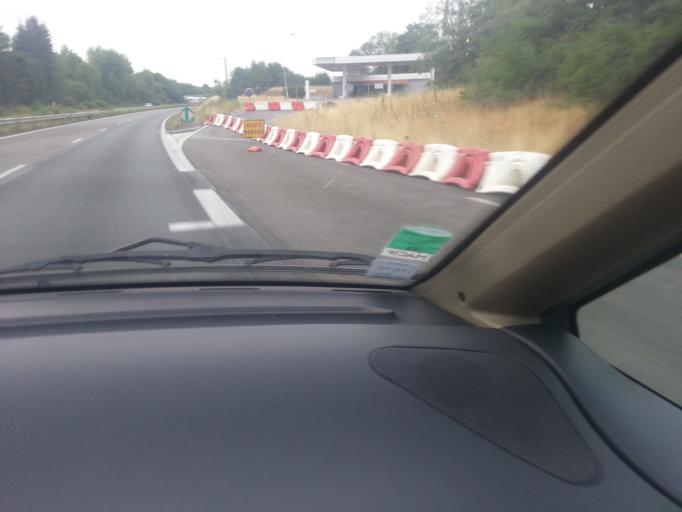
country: FR
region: Bourgogne
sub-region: Departement de Saone-et-Loire
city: Montceau-les-Mines
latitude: 46.6800
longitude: 4.3466
